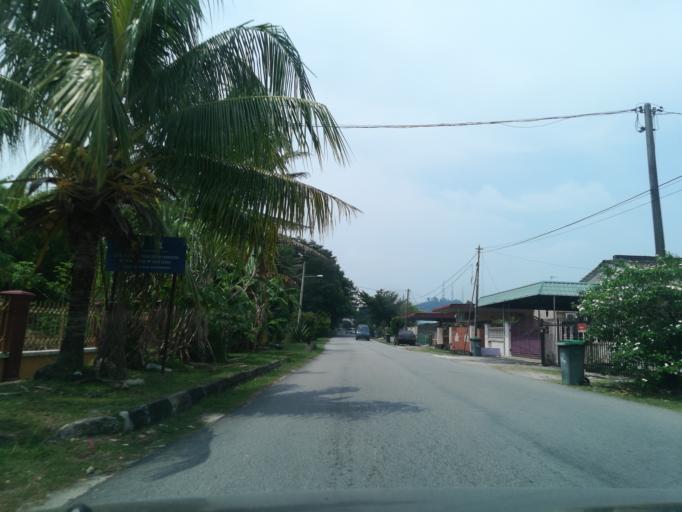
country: MY
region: Kedah
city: Kulim
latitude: 5.3989
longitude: 100.5592
